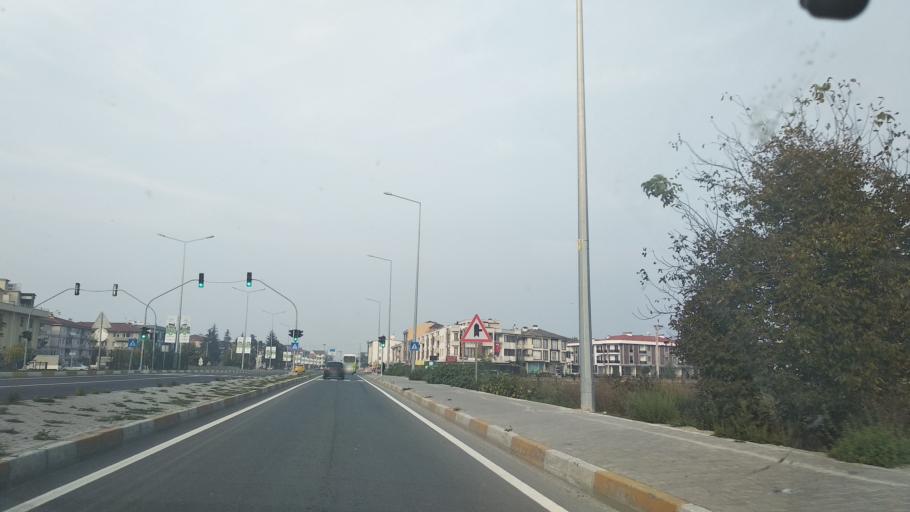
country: TR
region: Duzce
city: Duzce
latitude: 40.8321
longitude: 31.1686
